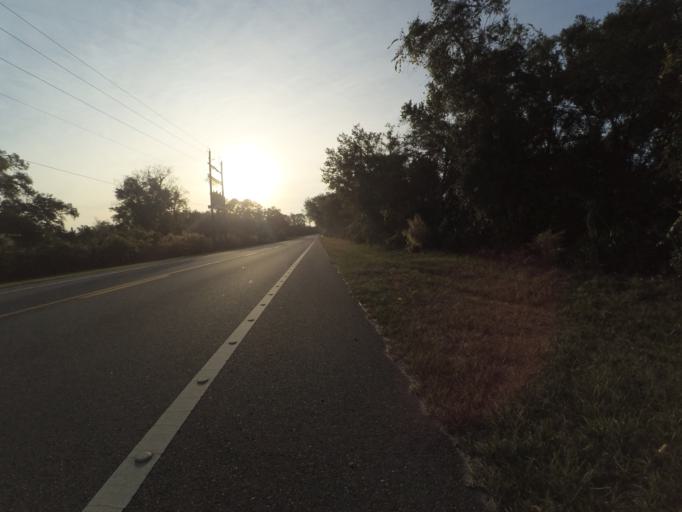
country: US
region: Florida
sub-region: Lake County
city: Umatilla
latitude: 28.9333
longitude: -81.6994
